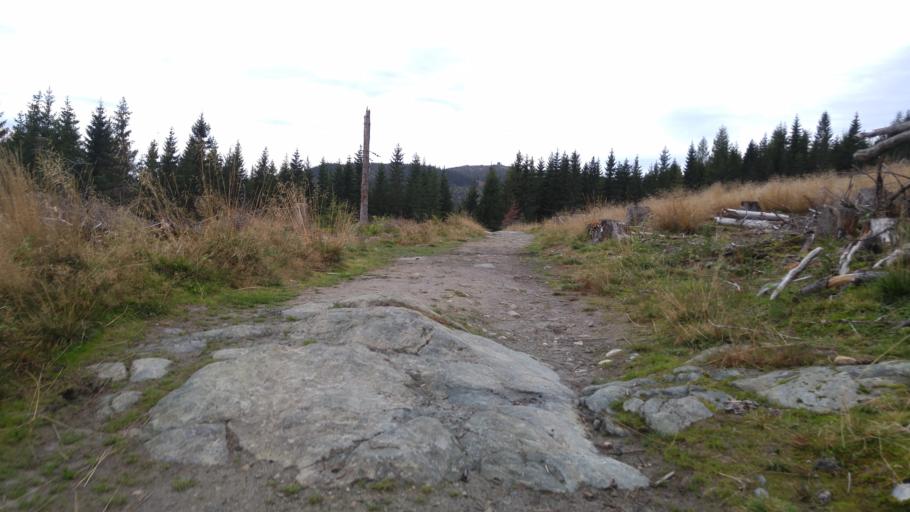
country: NO
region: Sor-Trondelag
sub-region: Trondheim
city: Trondheim
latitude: 63.4228
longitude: 10.3113
